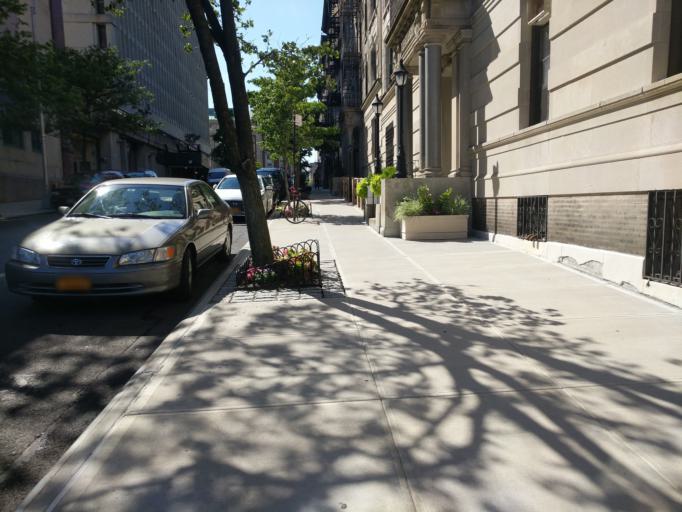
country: US
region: New York
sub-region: New York County
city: Manhattan
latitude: 40.8075
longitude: -73.9585
